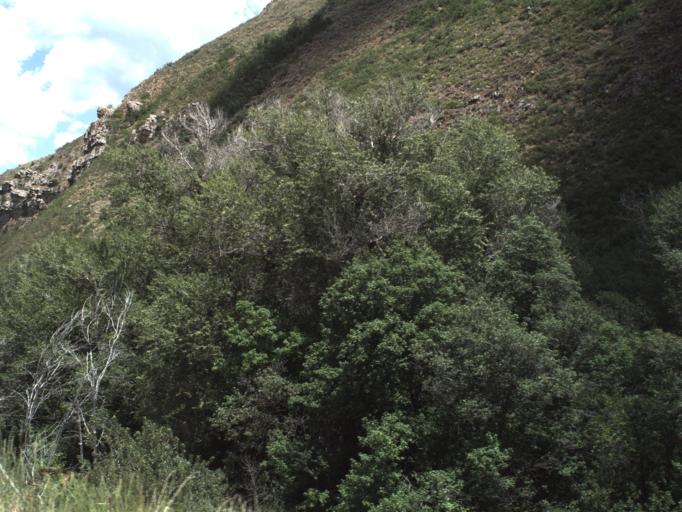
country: US
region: Utah
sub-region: Weber County
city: Wolf Creek
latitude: 41.3403
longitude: -111.6051
